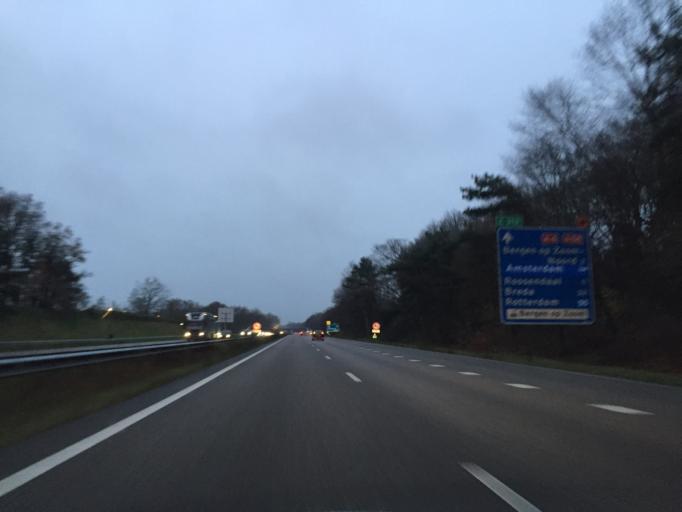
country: NL
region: North Brabant
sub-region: Gemeente Bergen op Zoom
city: Bergen op Zoom
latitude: 51.4842
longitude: 4.3165
